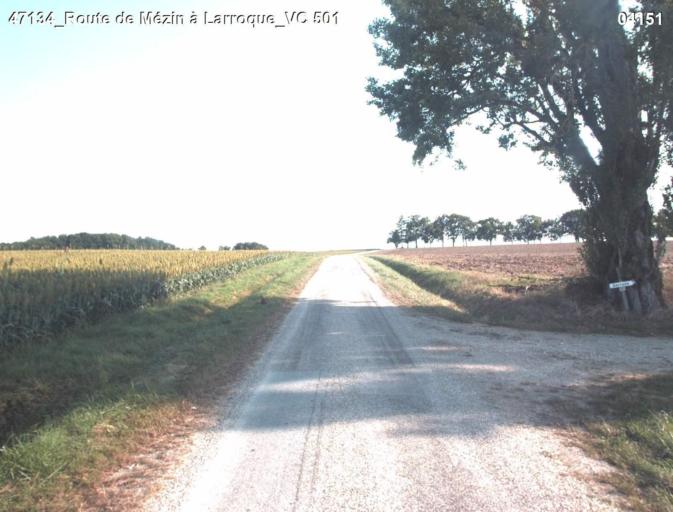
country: FR
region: Aquitaine
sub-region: Departement du Lot-et-Garonne
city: Mezin
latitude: 44.0316
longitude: 0.2677
